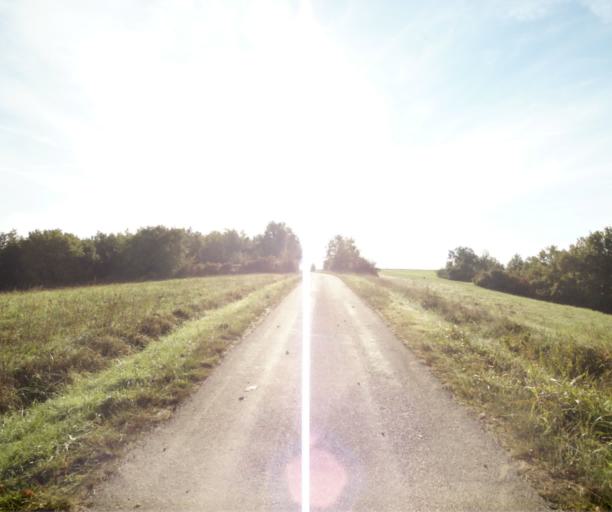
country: FR
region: Midi-Pyrenees
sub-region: Departement du Tarn-et-Garonne
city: Nohic
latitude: 43.9206
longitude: 1.4452
